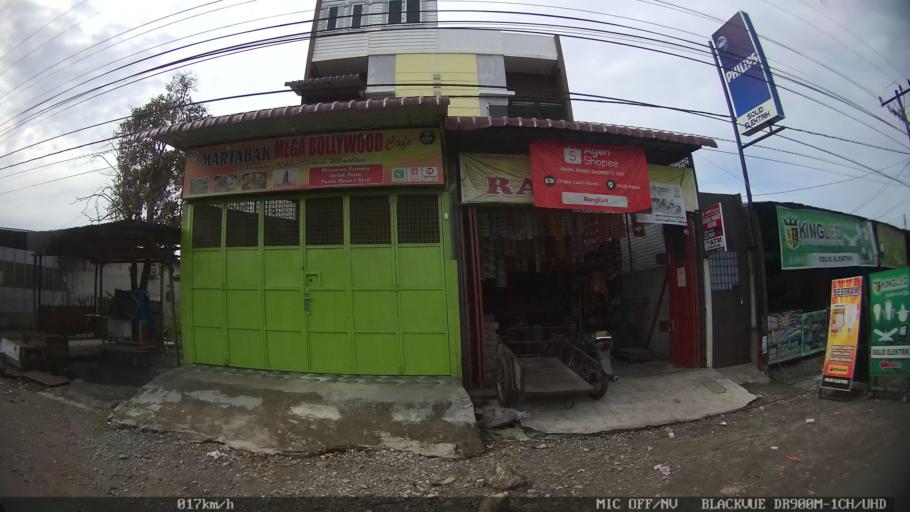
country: ID
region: North Sumatra
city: Medan
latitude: 3.6207
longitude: 98.7272
